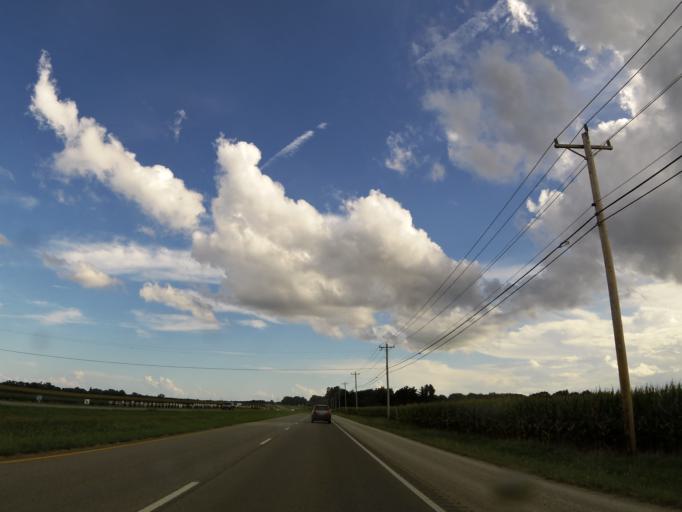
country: US
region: Kentucky
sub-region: Christian County
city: Hopkinsville
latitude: 36.7778
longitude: -87.4732
